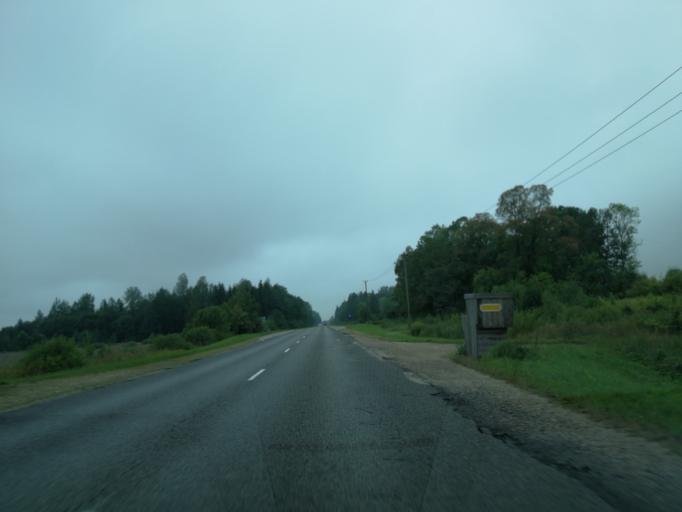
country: LV
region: Varkava
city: Vecvarkava
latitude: 56.3217
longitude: 26.4219
